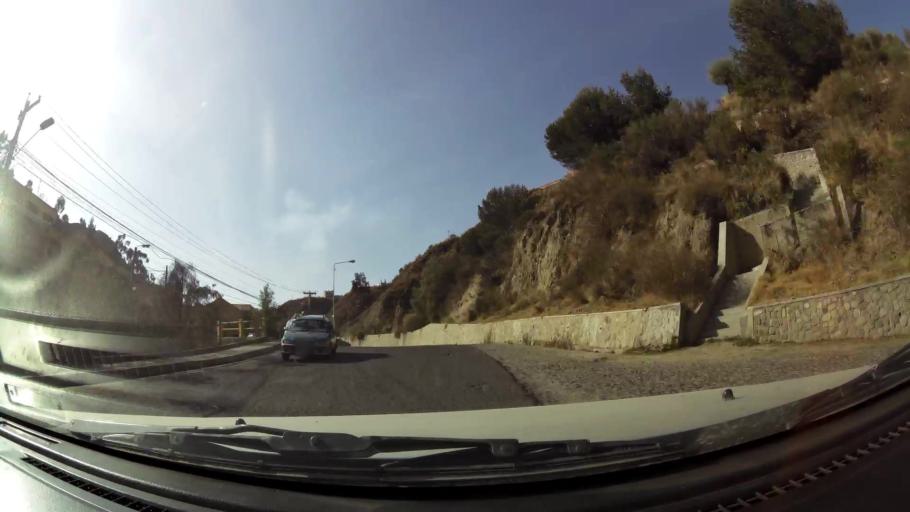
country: BO
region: La Paz
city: La Paz
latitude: -16.5290
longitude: -68.0782
